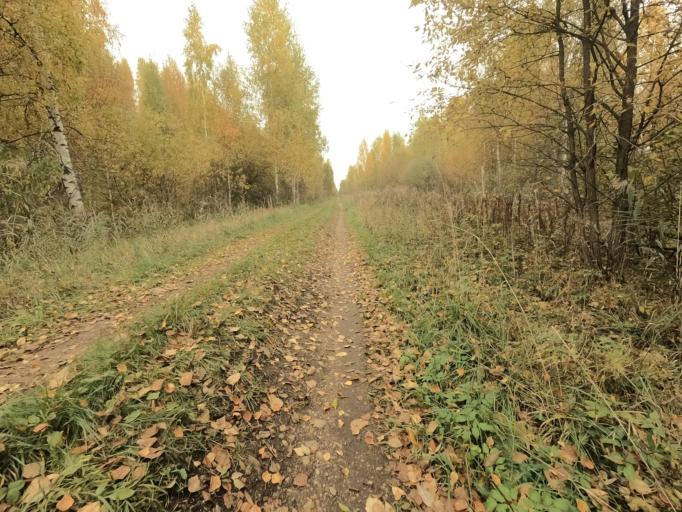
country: RU
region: Novgorod
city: Pankovka
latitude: 58.8871
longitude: 30.9473
